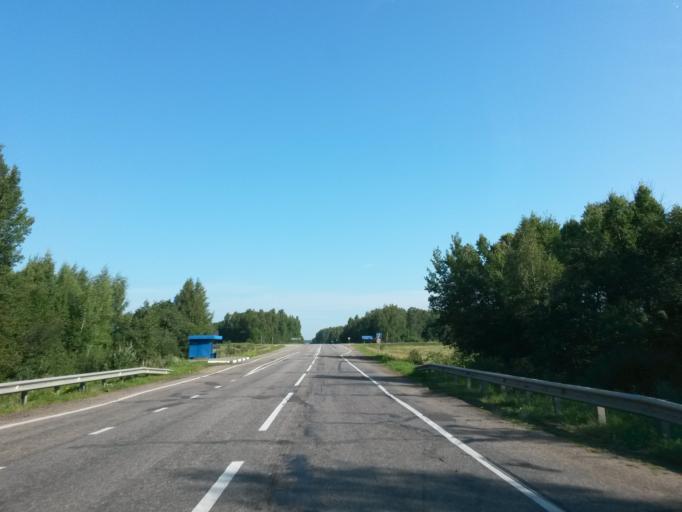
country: RU
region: Jaroslavl
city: Gavrilov-Yam
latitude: 57.4083
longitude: 39.9210
